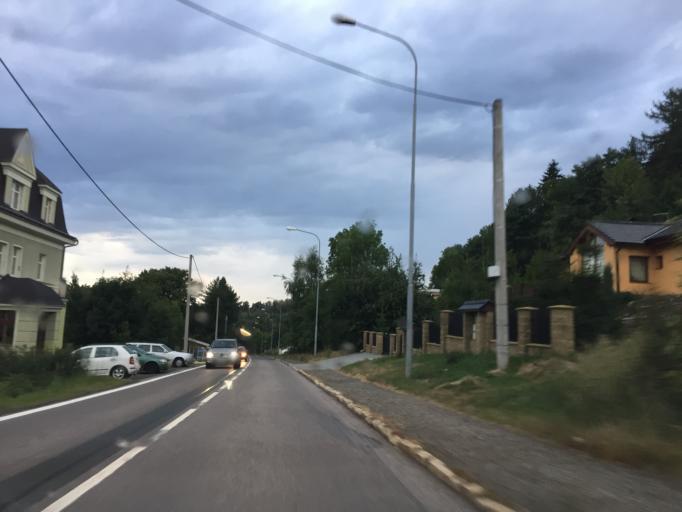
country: CZ
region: Liberecky
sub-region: Okres Jablonec nad Nisou
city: Jablonec nad Nisou
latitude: 50.6998
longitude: 15.1911
